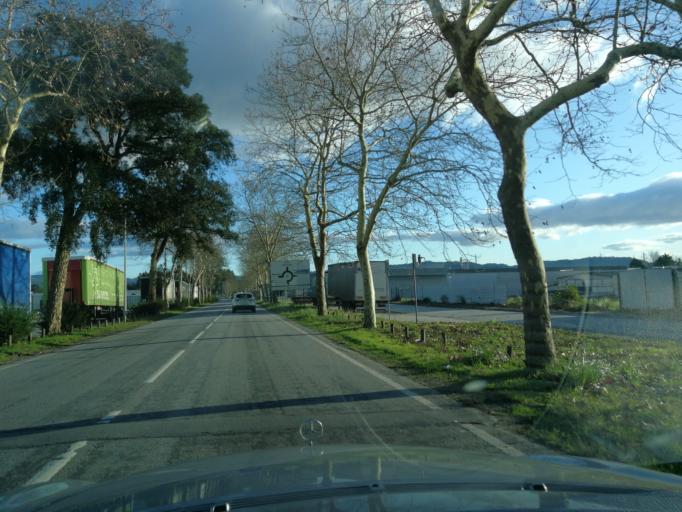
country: PT
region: Viana do Castelo
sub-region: Viana do Castelo
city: Darque
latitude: 41.6359
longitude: -8.7654
